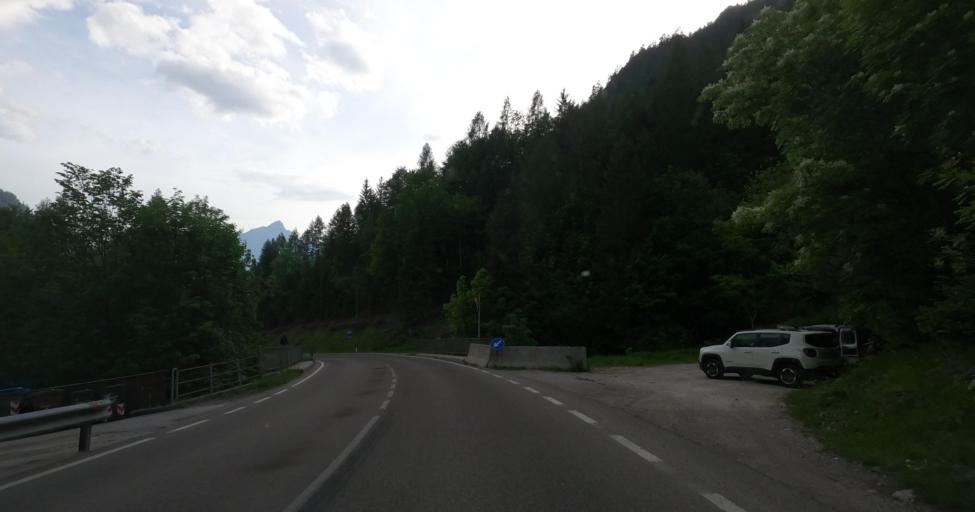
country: IT
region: Veneto
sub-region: Provincia di Belluno
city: Celat-San Tomaso Agordino
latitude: 46.3916
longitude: 11.9989
